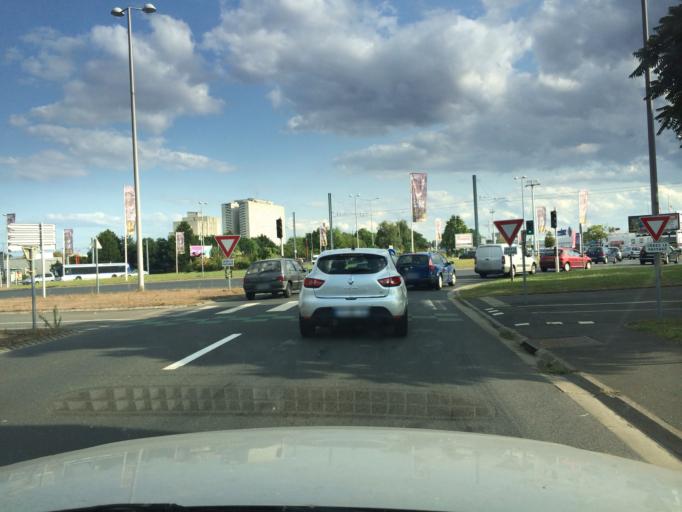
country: FR
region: Lower Normandy
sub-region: Departement du Calvados
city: Epron
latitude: 49.2117
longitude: -0.3638
